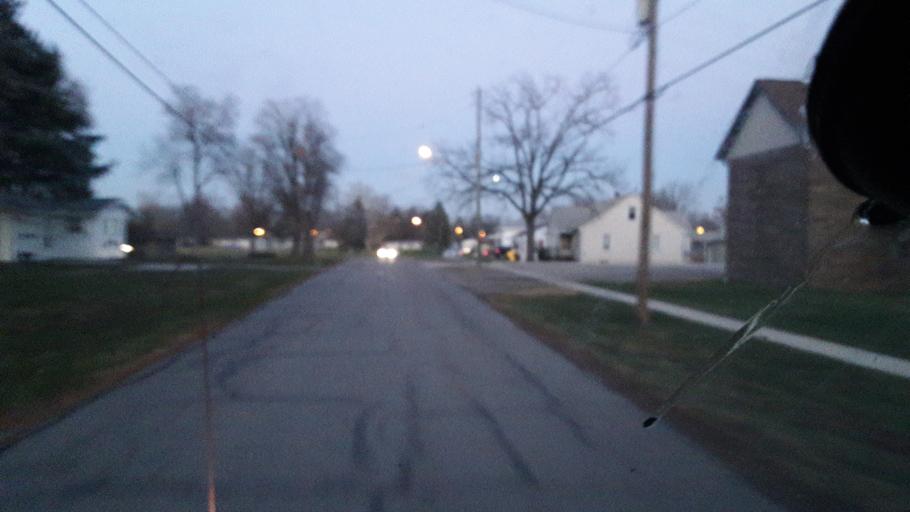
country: US
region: Ohio
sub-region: Defiance County
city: Hicksville
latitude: 41.2928
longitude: -84.7706
